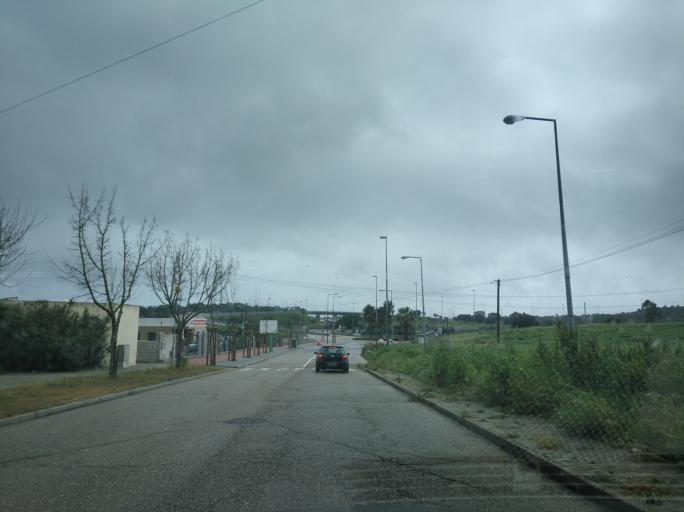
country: PT
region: Setubal
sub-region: Grandola
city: Grandola
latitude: 38.1702
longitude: -8.5561
